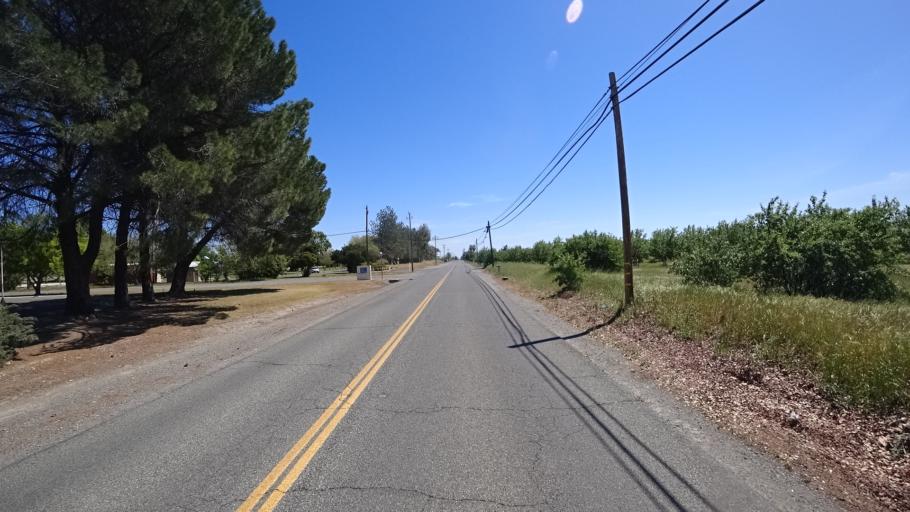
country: US
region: California
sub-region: Glenn County
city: Orland
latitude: 39.7379
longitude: -122.1729
